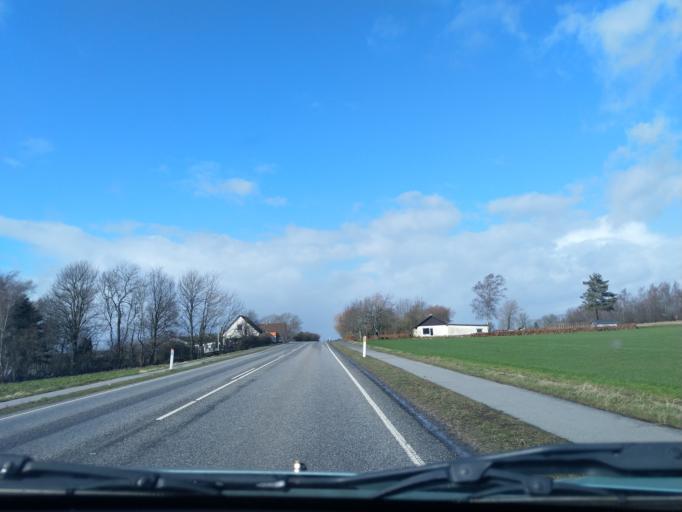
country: DK
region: Zealand
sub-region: Naestved Kommune
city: Naestved
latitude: 55.2868
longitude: 11.7085
